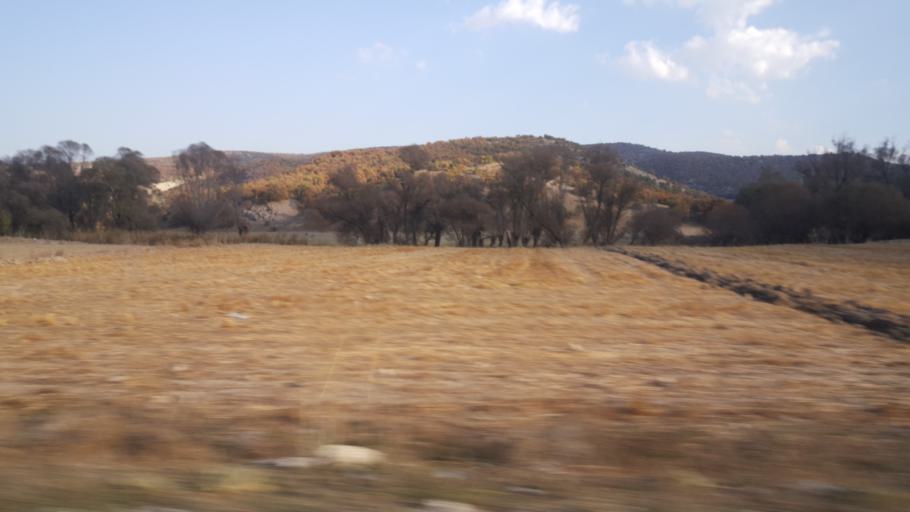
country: TR
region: Eskisehir
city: Kirka
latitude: 39.3644
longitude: 30.5880
